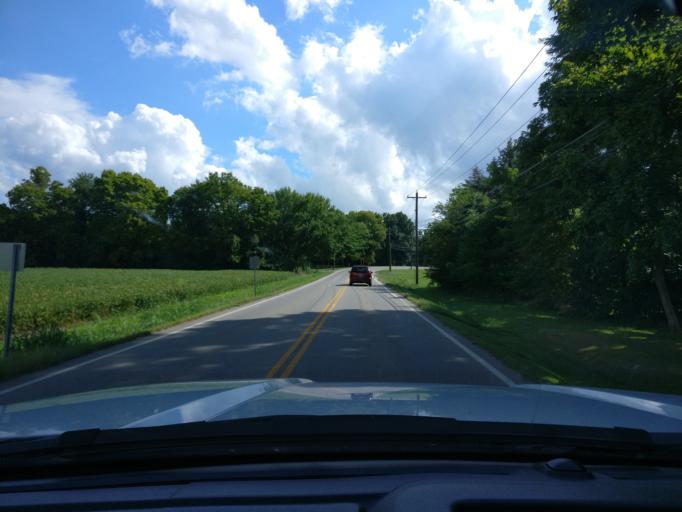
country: US
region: Ohio
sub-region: Warren County
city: Five Points
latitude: 39.5267
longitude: -84.1771
